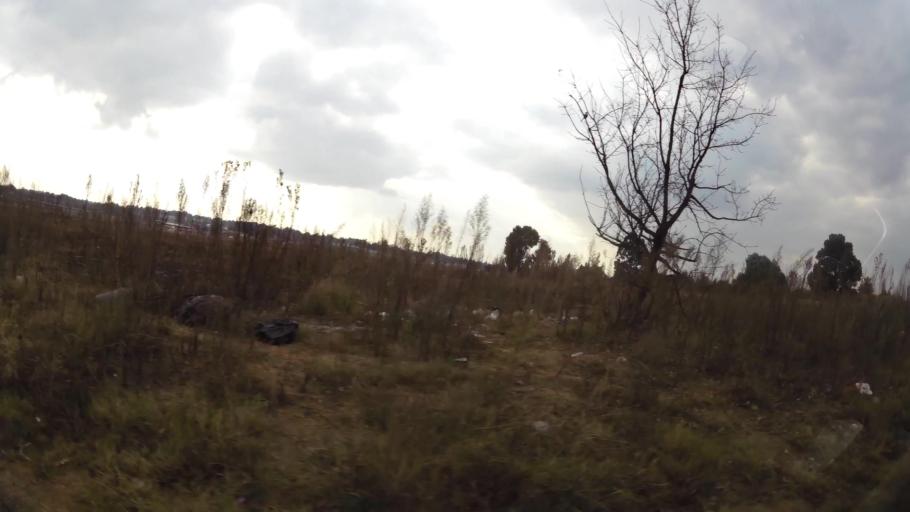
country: ZA
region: Gauteng
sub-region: Ekurhuleni Metropolitan Municipality
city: Benoni
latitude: -26.1373
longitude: 28.3588
